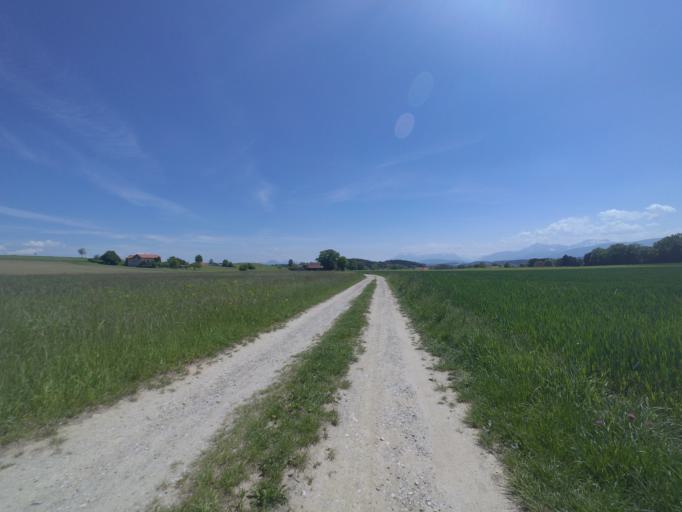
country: DE
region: Bavaria
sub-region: Upper Bavaria
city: Petting
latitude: 47.9391
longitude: 12.7985
